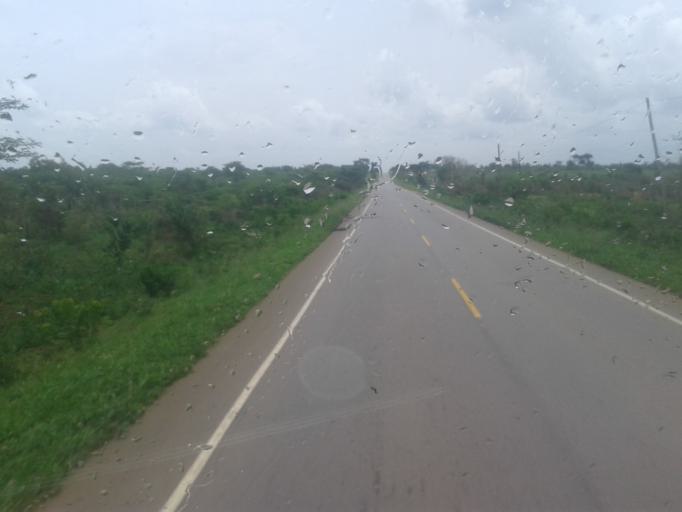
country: UG
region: Western Region
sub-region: Kiryandongo District
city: Masindi Port
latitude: 1.7518
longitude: 32.0220
